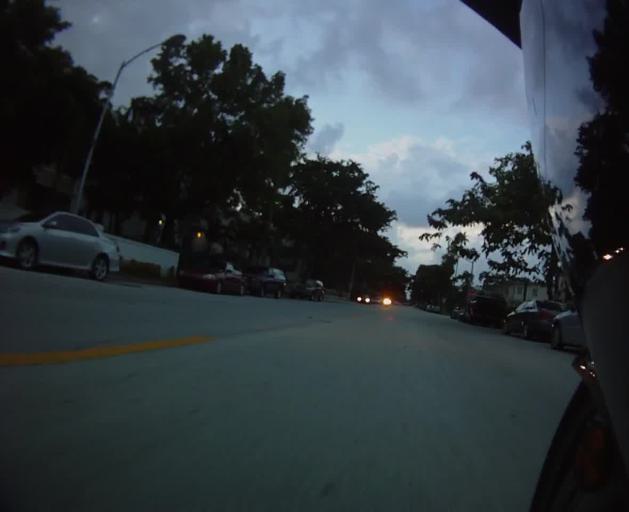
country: US
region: Florida
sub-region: Miami-Dade County
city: Miami Beach
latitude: 25.7777
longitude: -80.1384
